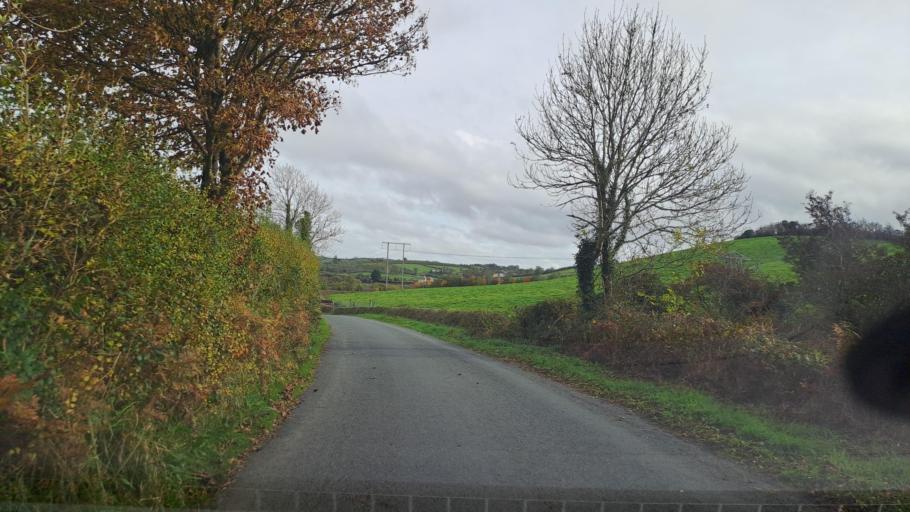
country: IE
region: Ulster
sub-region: An Cabhan
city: Bailieborough
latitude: 54.0216
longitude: -6.9191
